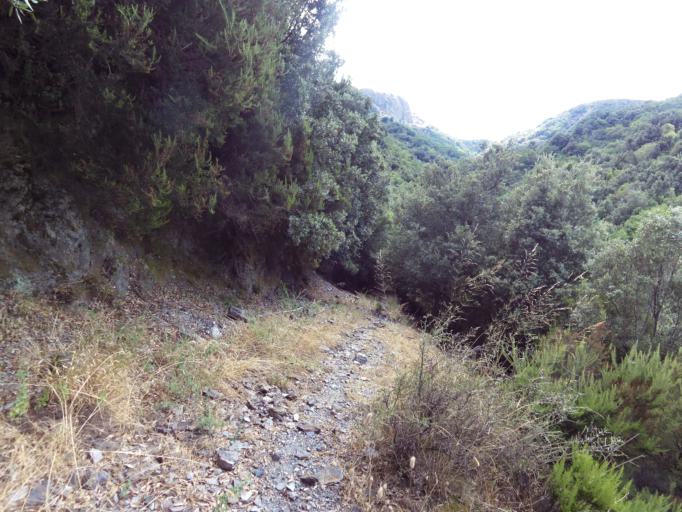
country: IT
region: Calabria
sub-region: Provincia di Reggio Calabria
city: Pazzano
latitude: 38.4699
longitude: 16.4321
